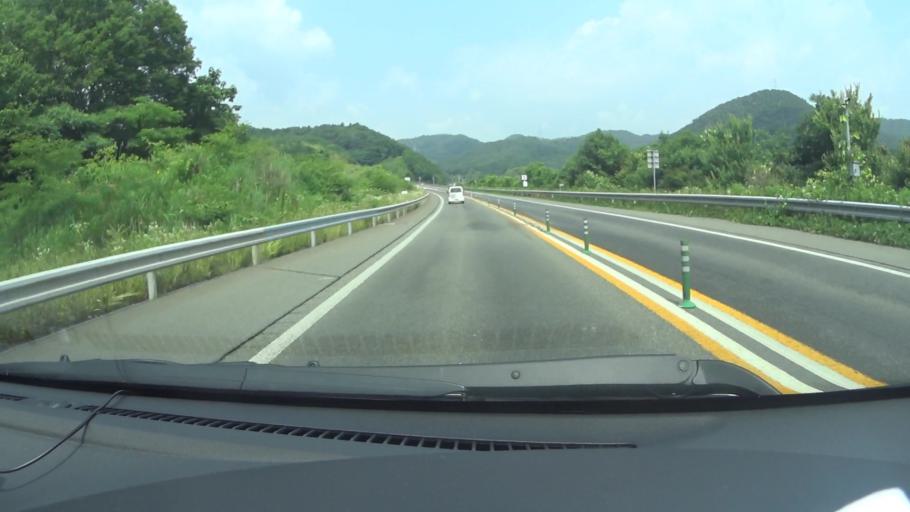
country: JP
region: Kyoto
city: Kameoka
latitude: 35.1268
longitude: 135.4749
